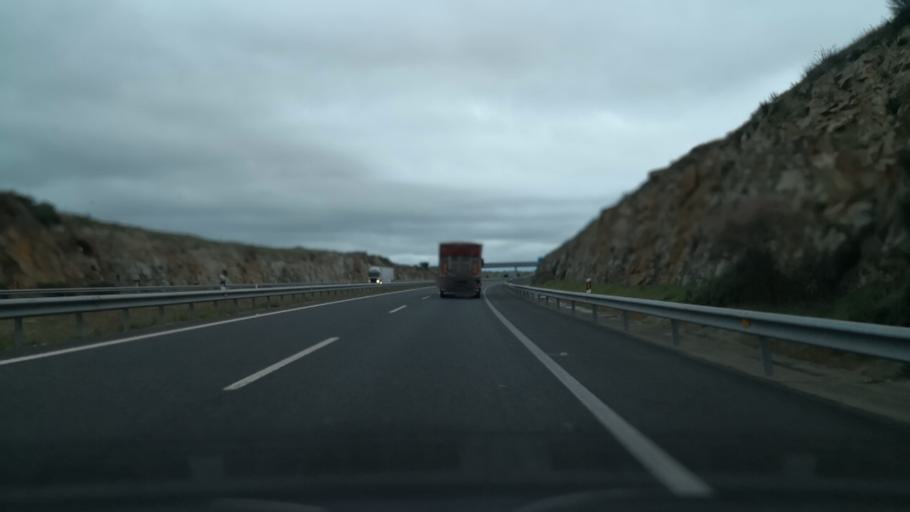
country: ES
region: Extremadura
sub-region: Provincia de Caceres
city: Caceres
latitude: 39.4478
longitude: -6.4138
